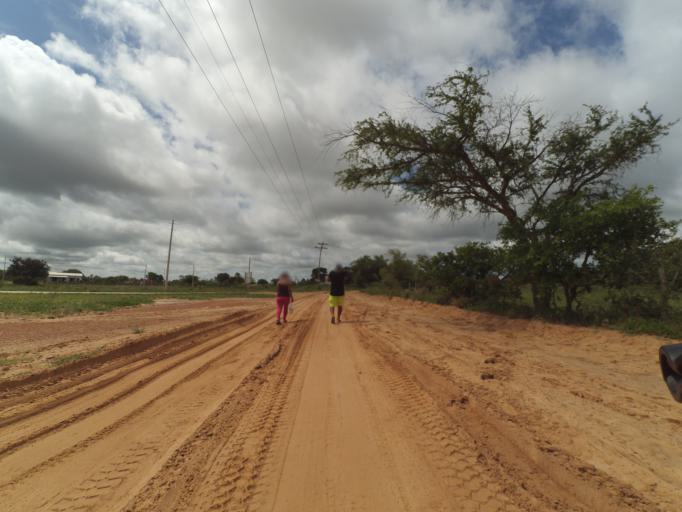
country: BO
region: Santa Cruz
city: Santa Rita
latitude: -17.9047
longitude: -63.2433
